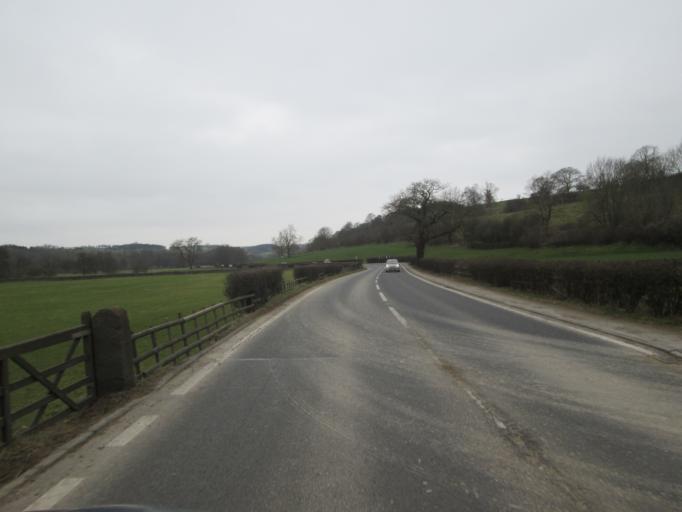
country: GB
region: England
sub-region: Derbyshire
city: Bakewell
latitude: 53.1897
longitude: -1.6291
